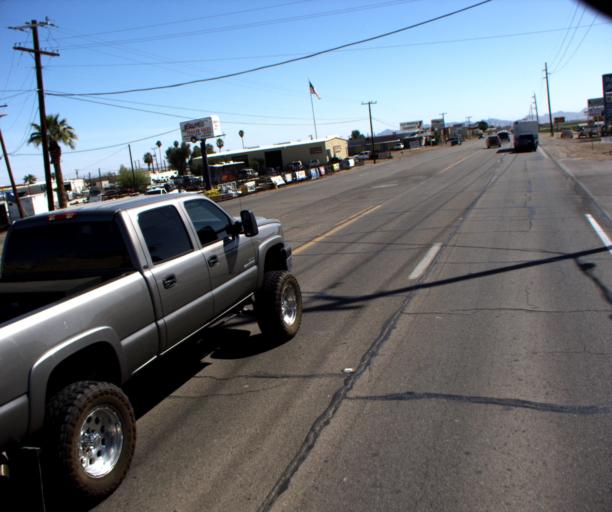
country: US
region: Arizona
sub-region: Yuma County
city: Yuma
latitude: 32.6986
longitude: -114.5949
